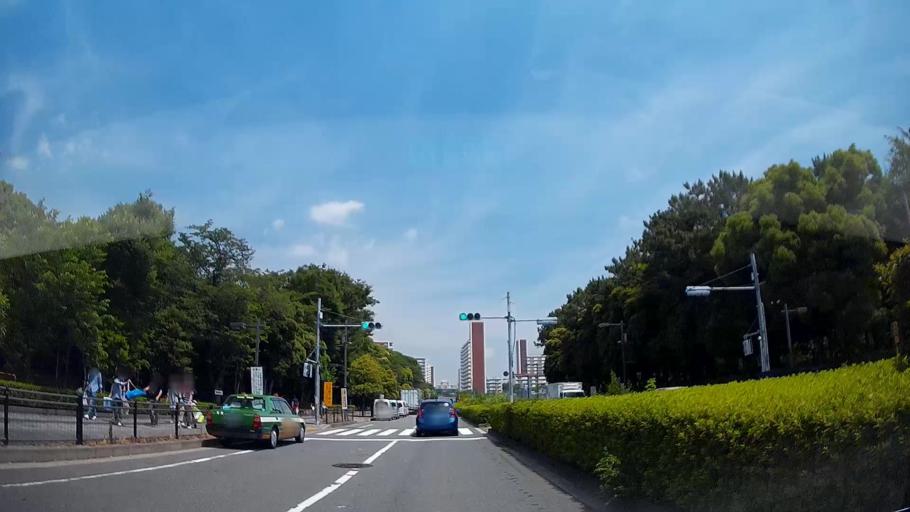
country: JP
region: Kanagawa
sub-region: Kawasaki-shi
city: Kawasaki
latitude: 35.5934
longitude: 139.7509
